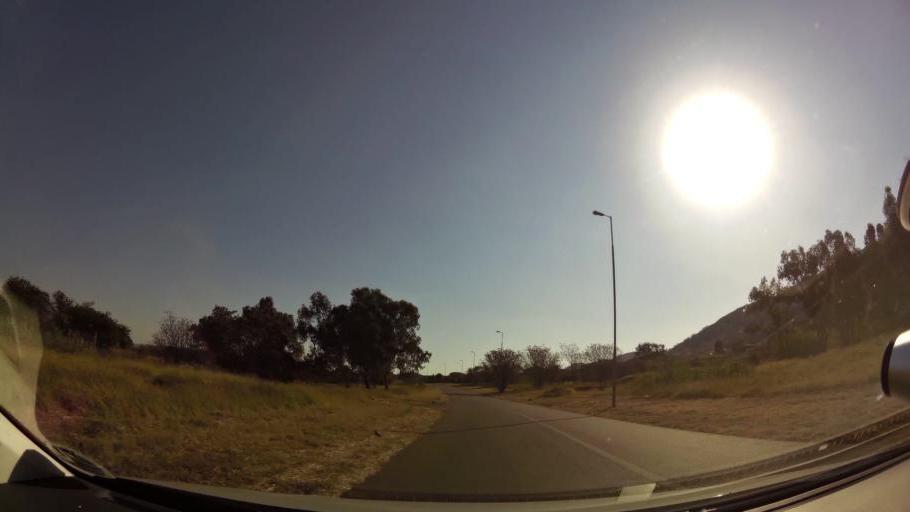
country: ZA
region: Gauteng
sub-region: City of Tshwane Metropolitan Municipality
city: Pretoria
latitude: -25.6950
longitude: 28.1302
